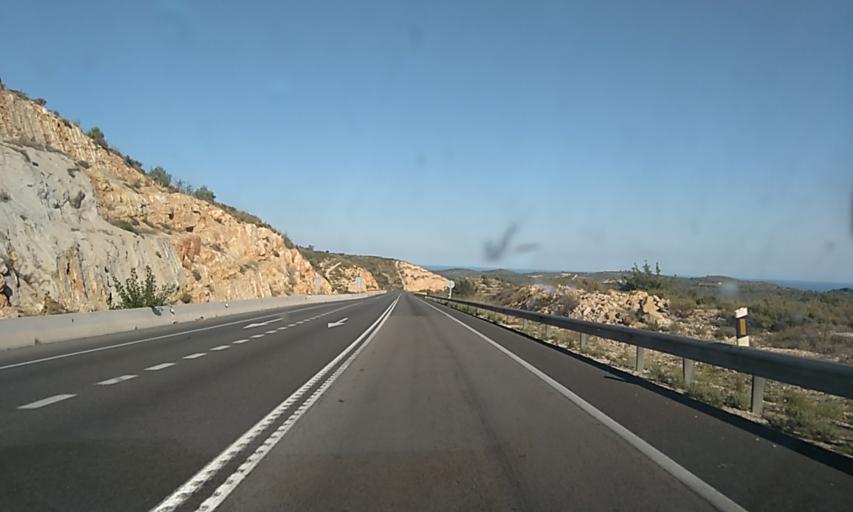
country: ES
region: Valencia
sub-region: Provincia de Castello
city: Torreblanca
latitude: 40.2106
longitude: 0.1193
